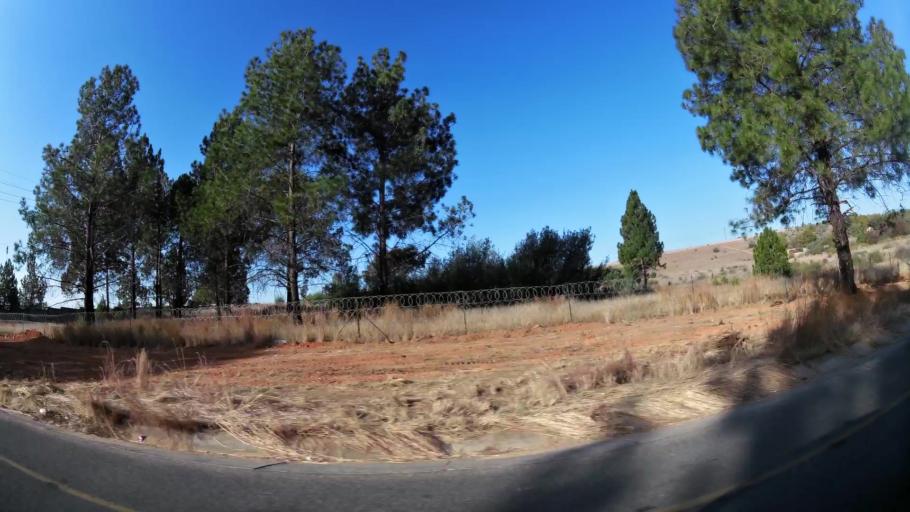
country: ZA
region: Gauteng
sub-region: West Rand District Municipality
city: Muldersdriseloop
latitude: -26.0300
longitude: 27.9089
